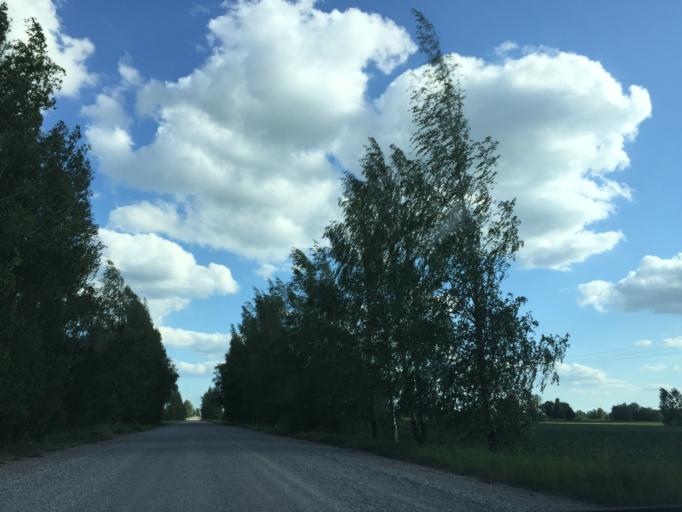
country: LV
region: Kandava
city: Kandava
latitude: 56.9204
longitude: 22.7893
